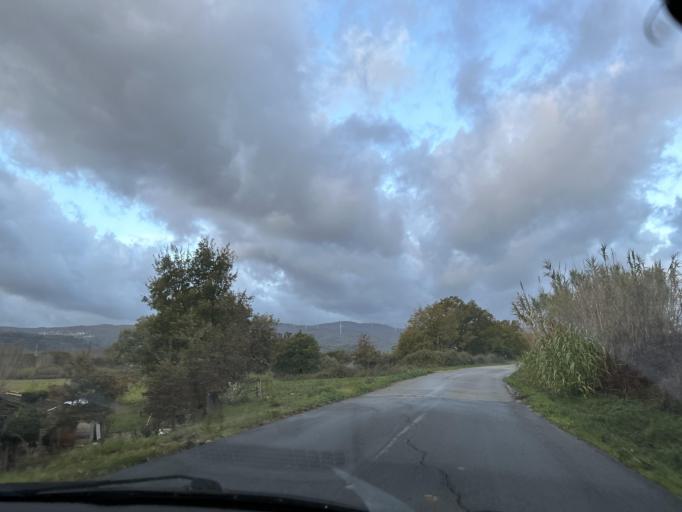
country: IT
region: Calabria
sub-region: Provincia di Catanzaro
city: Squillace
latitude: 38.7747
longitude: 16.4988
